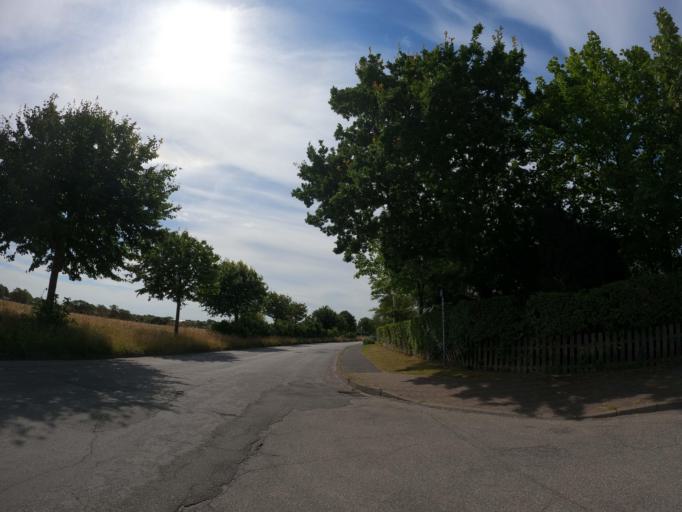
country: DE
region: Schleswig-Holstein
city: Westerland
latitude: 54.9207
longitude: 8.3188
